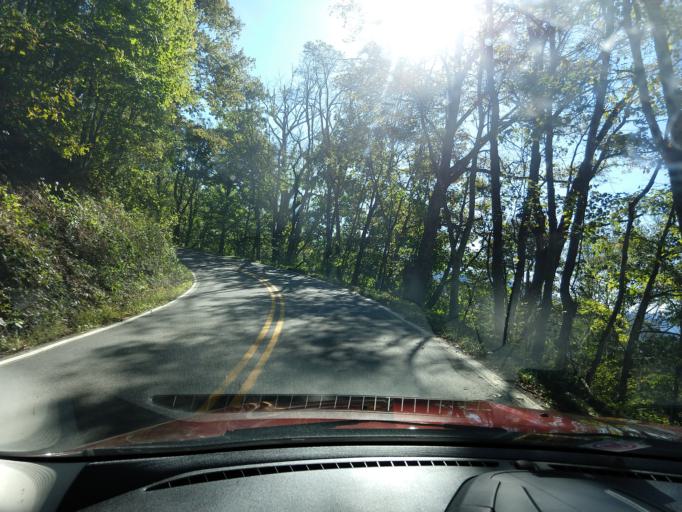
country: US
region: Virginia
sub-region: Alleghany County
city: Clifton Forge
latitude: 37.8833
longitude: -79.8880
